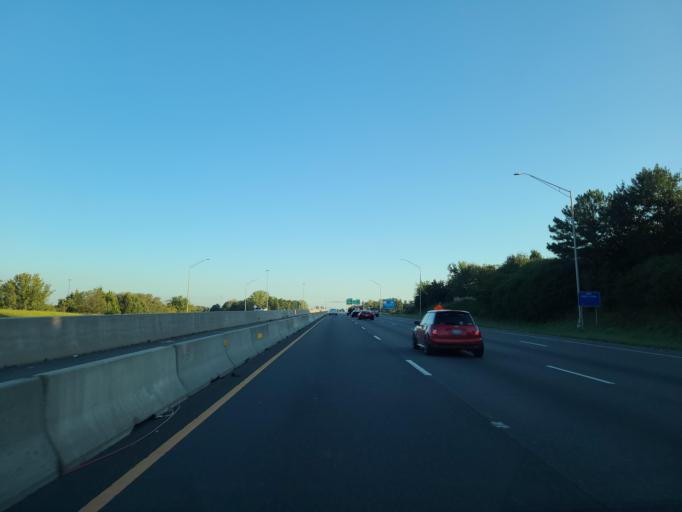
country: US
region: North Carolina
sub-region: Mecklenburg County
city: Pineville
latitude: 35.0809
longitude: -80.8728
